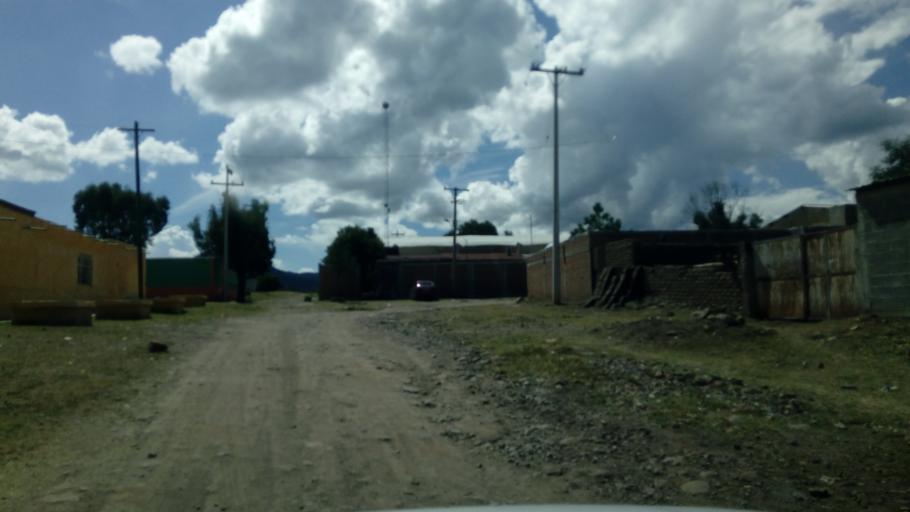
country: MX
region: Durango
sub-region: Durango
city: Jose Refugio Salcido
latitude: 23.7916
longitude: -104.4866
